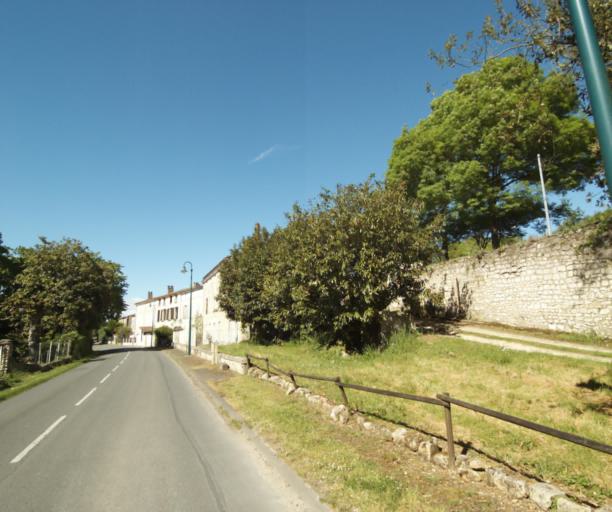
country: FR
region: Poitou-Charentes
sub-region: Departement de la Charente-Maritime
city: Bussac-sur-Charente
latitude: 45.8181
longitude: -0.6384
